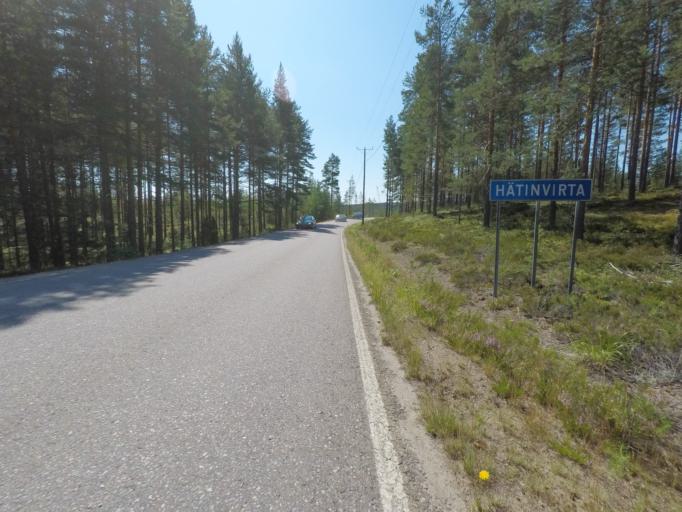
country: FI
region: Southern Savonia
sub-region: Mikkeli
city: Puumala
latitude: 61.4549
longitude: 28.1737
